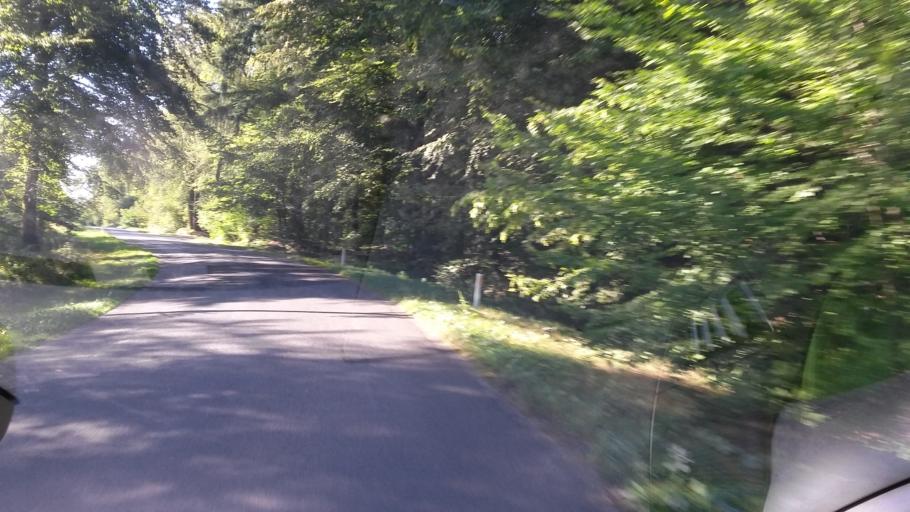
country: BE
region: Wallonia
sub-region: Province du Luxembourg
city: Neufchateau
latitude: 49.8043
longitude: 5.4141
